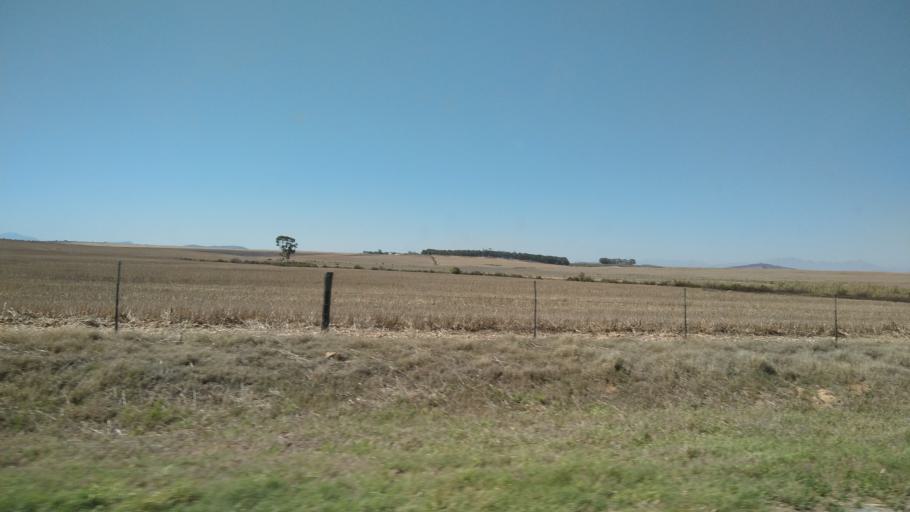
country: ZA
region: Western Cape
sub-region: West Coast District Municipality
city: Moorreesburg
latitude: -33.2146
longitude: 18.5355
